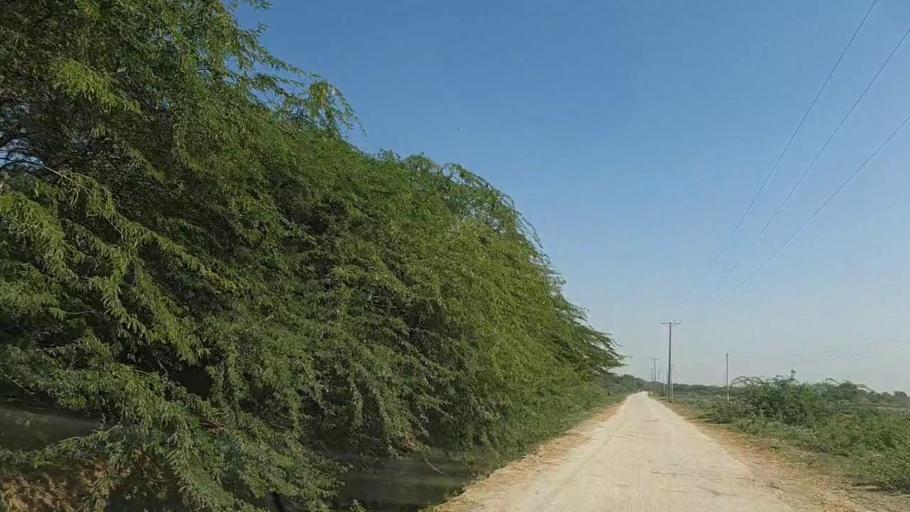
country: PK
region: Sindh
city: Daro Mehar
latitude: 24.7882
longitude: 68.1680
